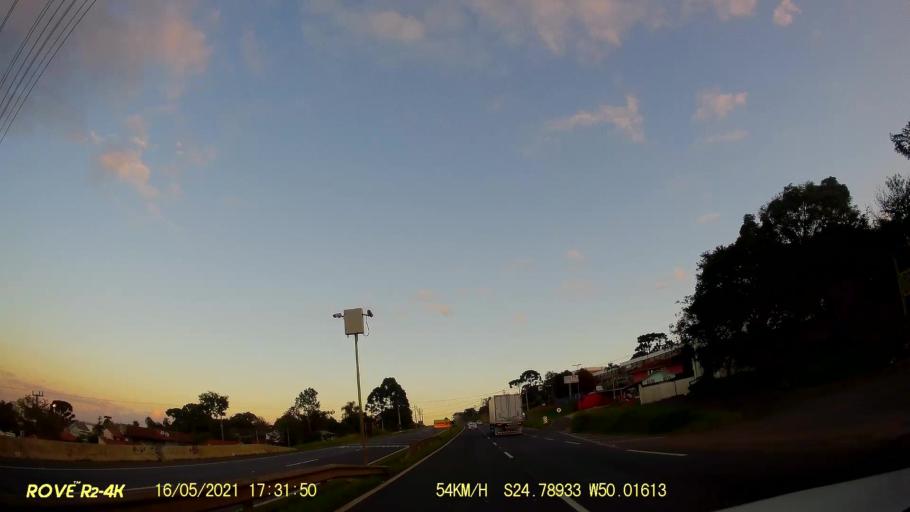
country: BR
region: Parana
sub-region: Castro
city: Castro
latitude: -24.7895
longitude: -50.0161
